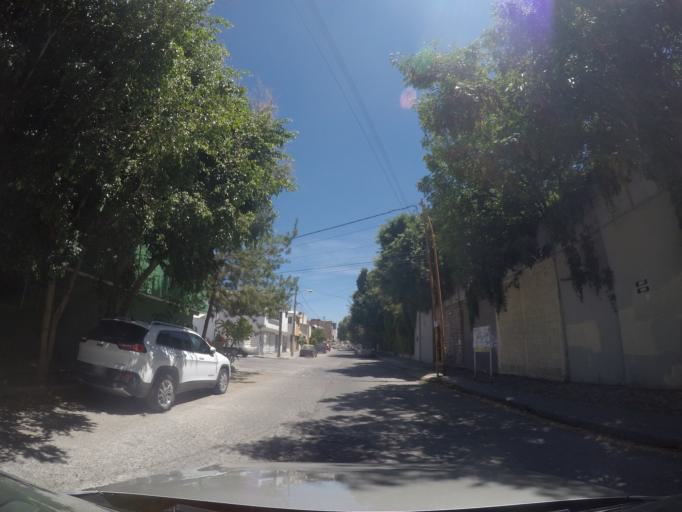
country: MX
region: San Luis Potosi
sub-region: San Luis Potosi
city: San Luis Potosi
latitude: 22.1582
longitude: -100.9942
